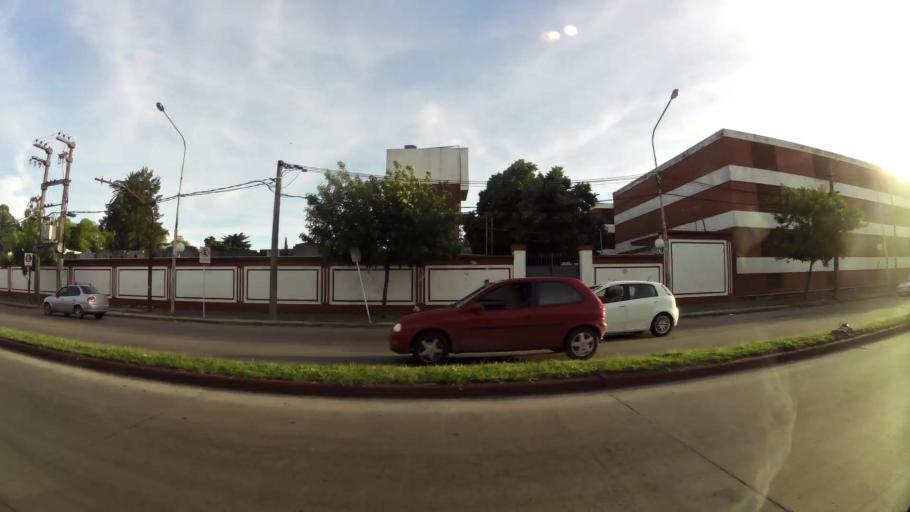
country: AR
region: Buenos Aires
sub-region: Partido de Moron
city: Moron
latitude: -34.6609
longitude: -58.6265
